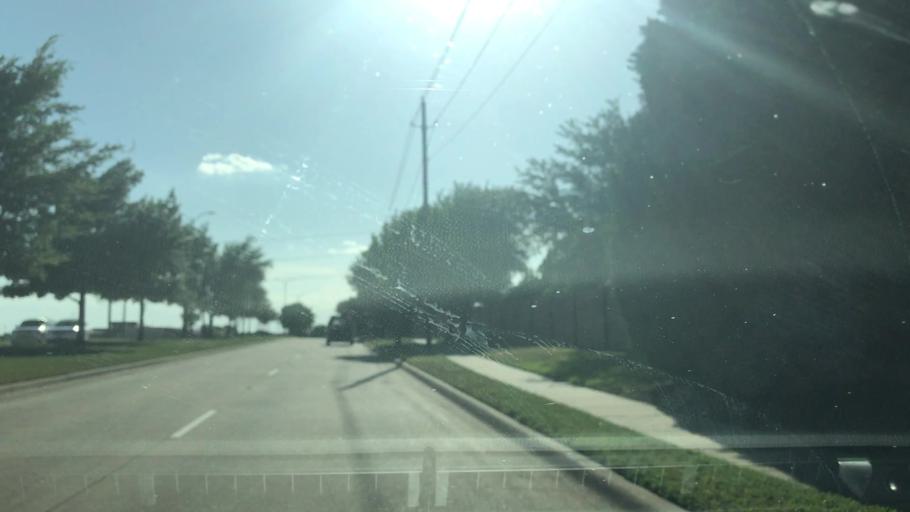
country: US
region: Texas
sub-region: Collin County
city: Frisco
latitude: 33.1161
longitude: -96.7732
